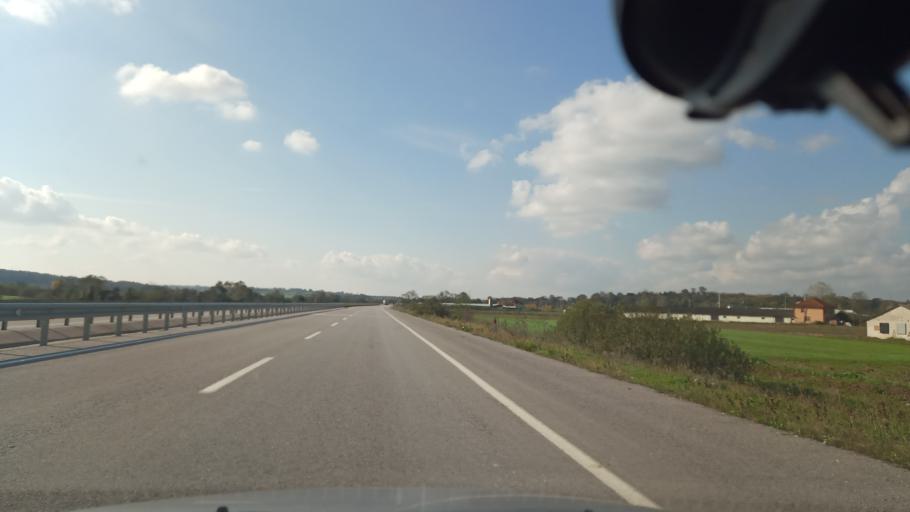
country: TR
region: Sakarya
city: Kaynarca
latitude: 41.0762
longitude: 30.4043
